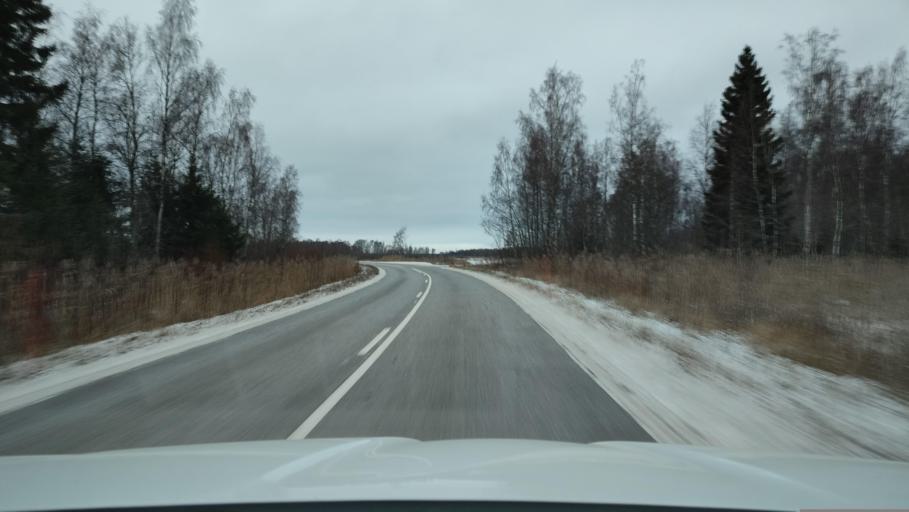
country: FI
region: Ostrobothnia
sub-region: Vaasa
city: Replot
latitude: 63.2798
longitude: 21.3409
